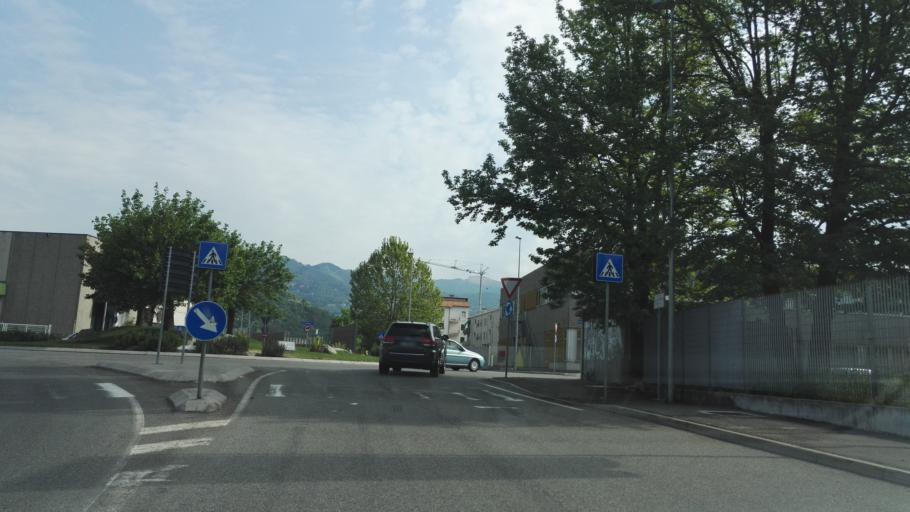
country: IT
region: Lombardy
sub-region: Provincia di Como
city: Como
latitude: 45.7814
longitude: 9.0797
